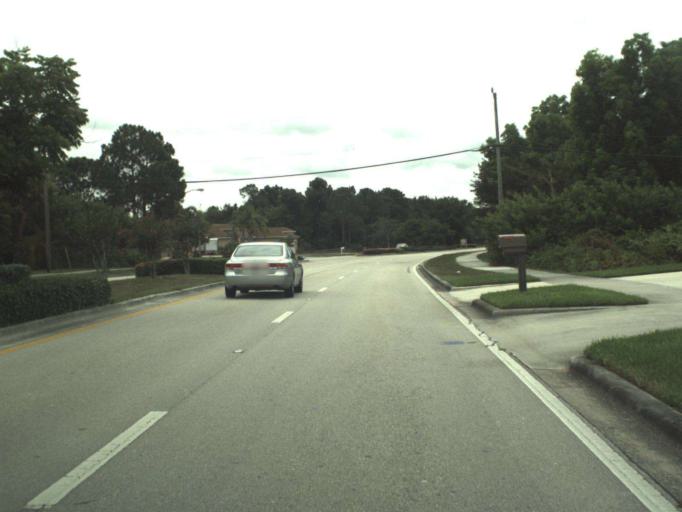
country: US
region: Florida
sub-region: Saint Lucie County
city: River Park
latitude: 27.3283
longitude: -80.3504
